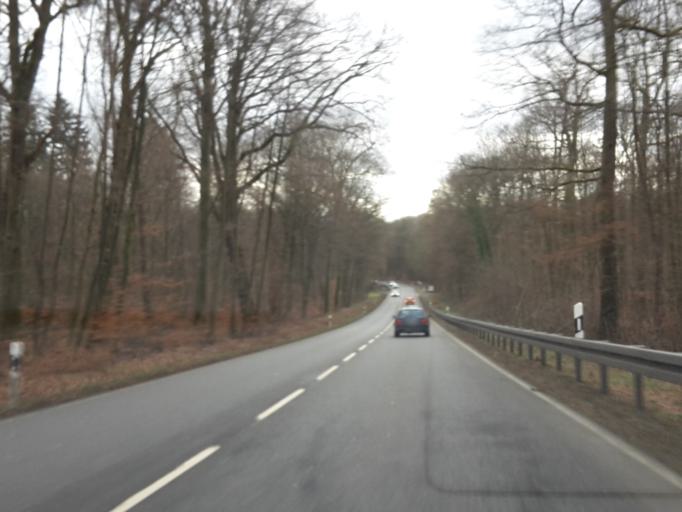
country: DE
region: Hesse
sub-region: Regierungsbezirk Darmstadt
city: Wiesbaden
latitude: 50.1125
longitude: 8.2097
